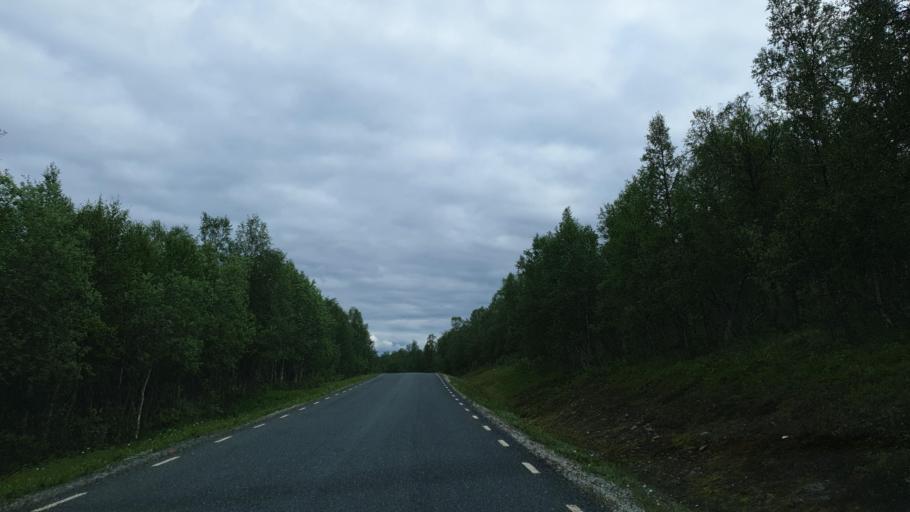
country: NO
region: Nordland
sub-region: Hattfjelldal
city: Hattfjelldal
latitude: 65.4225
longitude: 14.9084
